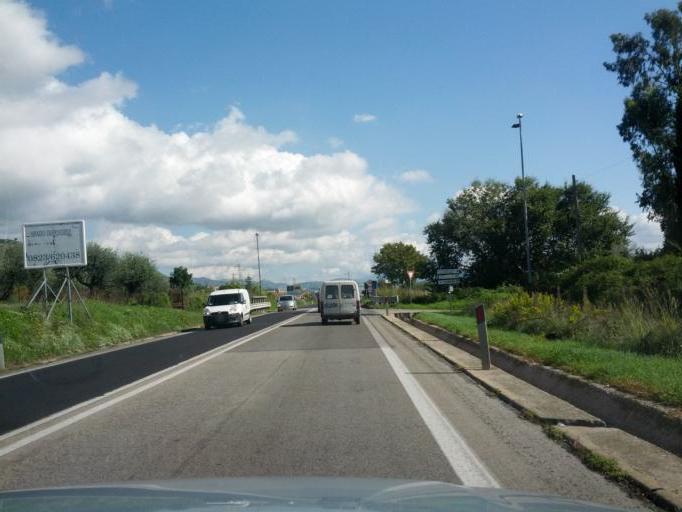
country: IT
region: Latium
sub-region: Provincia di Latina
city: Formia
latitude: 41.2669
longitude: 13.6617
